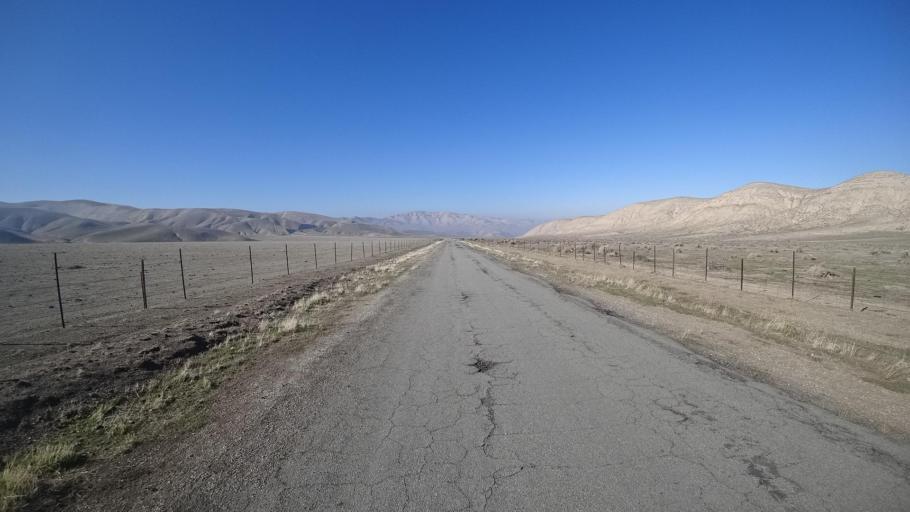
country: US
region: California
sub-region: Kern County
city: Maricopa
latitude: 34.9959
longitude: -119.3962
